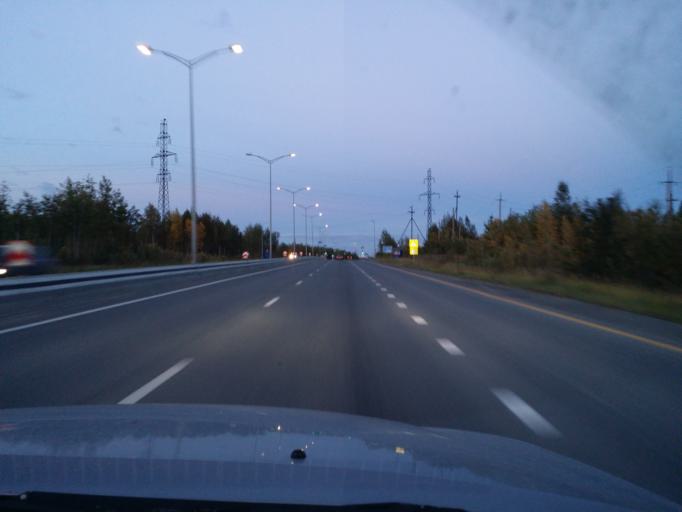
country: RU
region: Khanty-Mansiyskiy Avtonomnyy Okrug
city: Nizhnevartovsk
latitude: 60.9876
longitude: 76.4544
